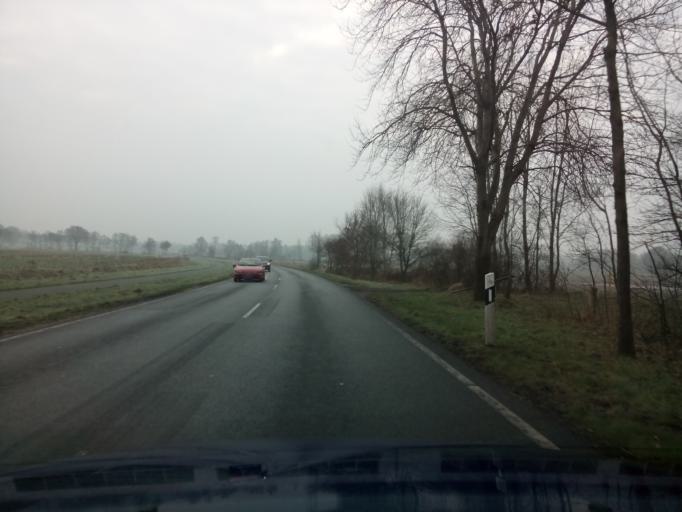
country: DE
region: Lower Saxony
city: Flogeln
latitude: 53.6215
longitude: 8.8174
